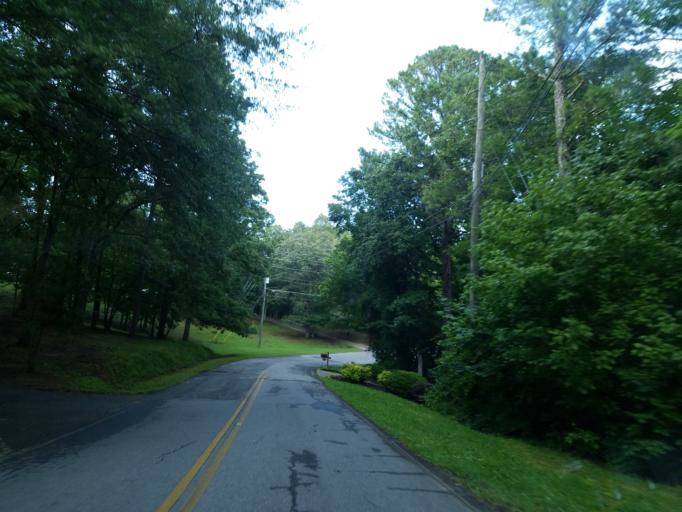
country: US
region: Georgia
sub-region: Bartow County
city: Emerson
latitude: 34.0938
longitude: -84.7563
